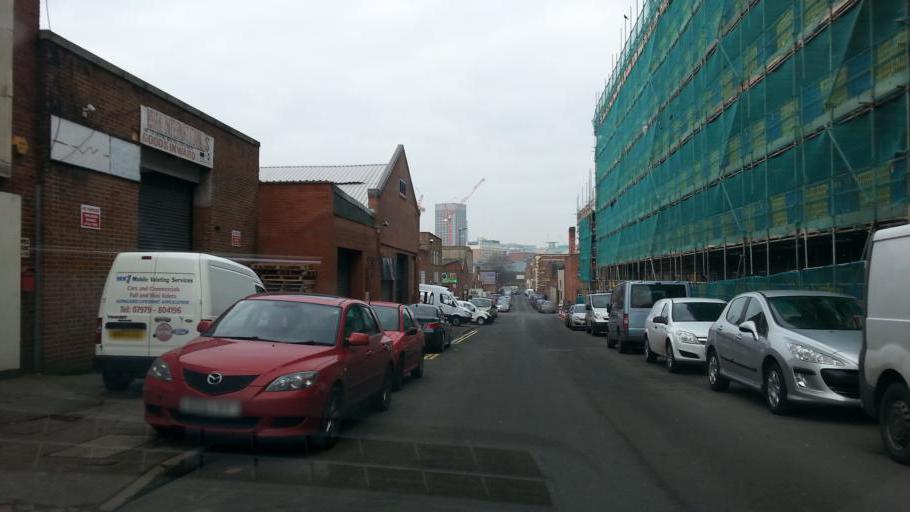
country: GB
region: England
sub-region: City and Borough of Birmingham
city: Birmingham
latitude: 52.4722
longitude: -1.8859
